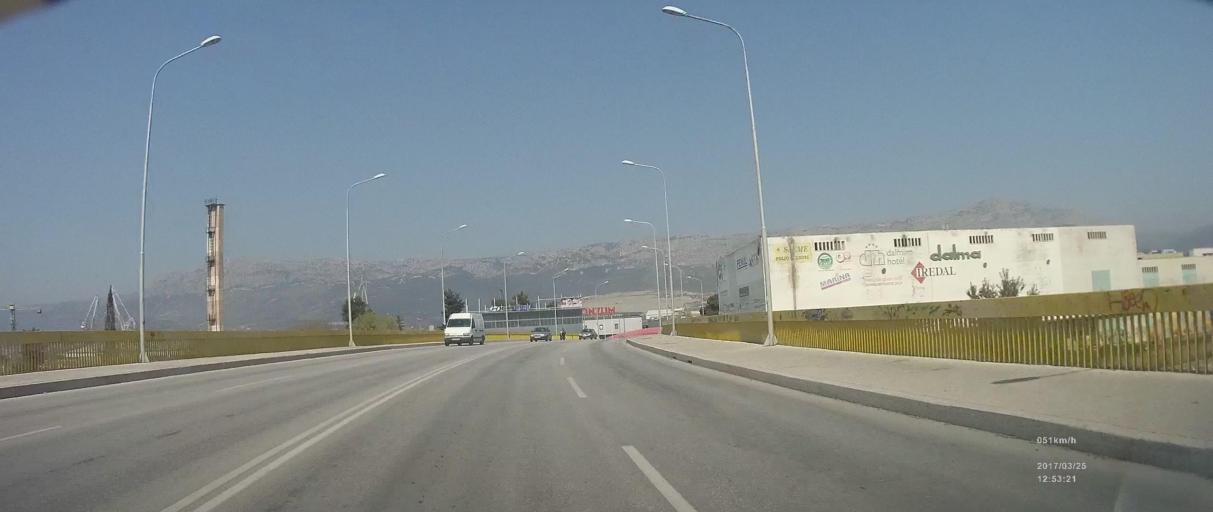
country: HR
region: Splitsko-Dalmatinska
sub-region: Grad Split
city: Split
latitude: 43.5217
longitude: 16.4485
